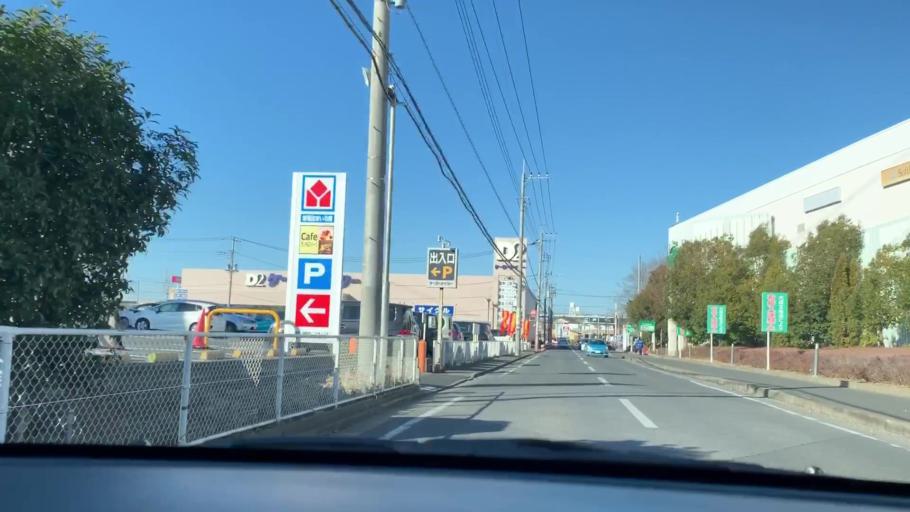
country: JP
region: Chiba
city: Kashiwa
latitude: 35.8822
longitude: 139.9678
